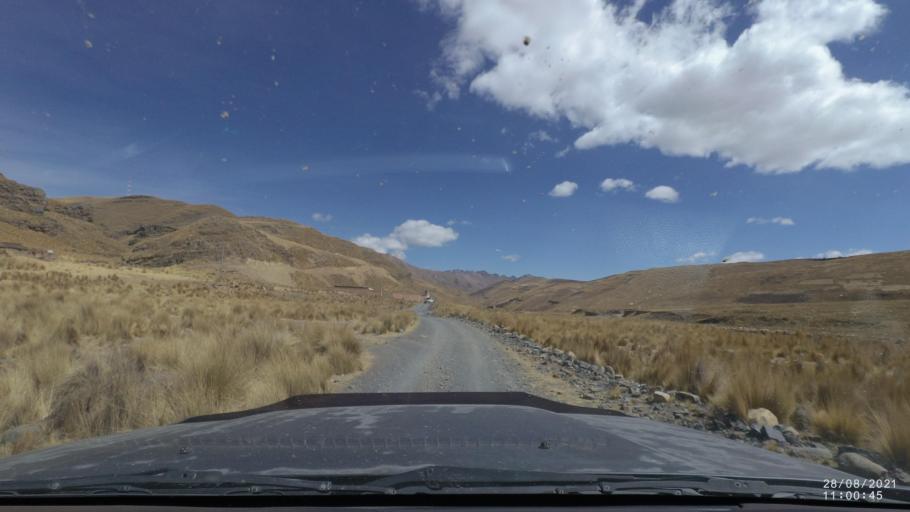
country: BO
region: Cochabamba
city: Cochabamba
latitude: -17.1824
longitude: -66.2623
